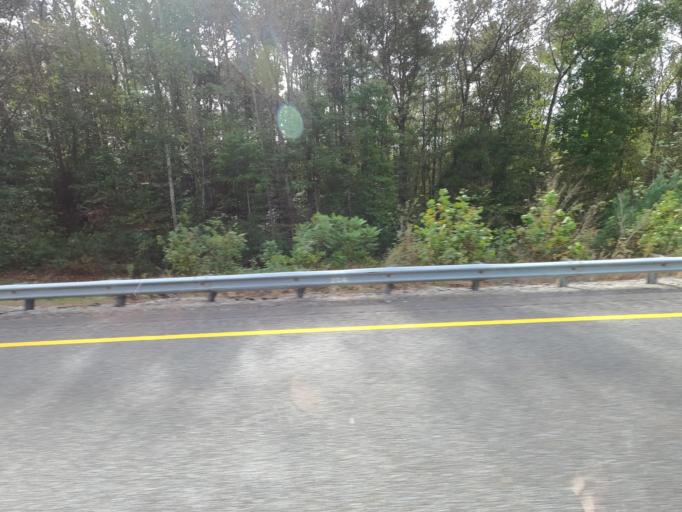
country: US
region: Tennessee
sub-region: Decatur County
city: Parsons
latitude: 35.8164
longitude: -88.2257
